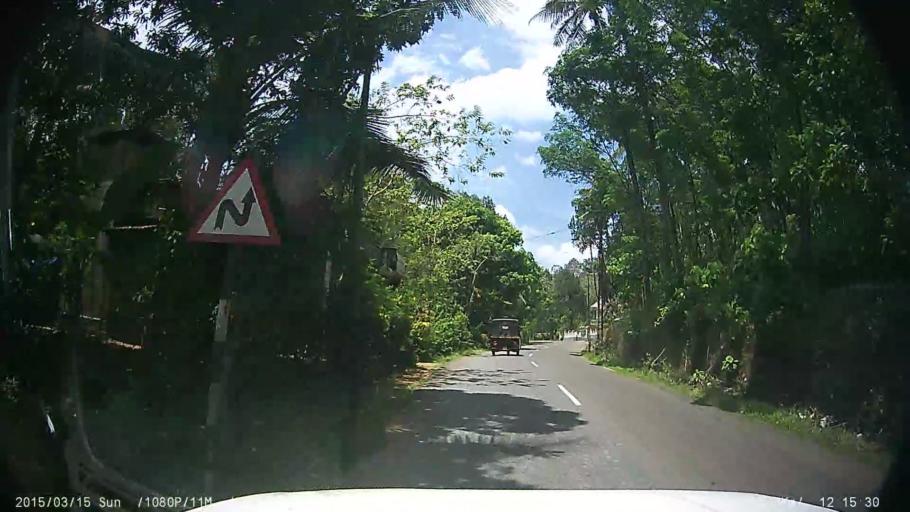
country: IN
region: Kerala
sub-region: Kottayam
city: Palackattumala
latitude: 9.7496
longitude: 76.6059
